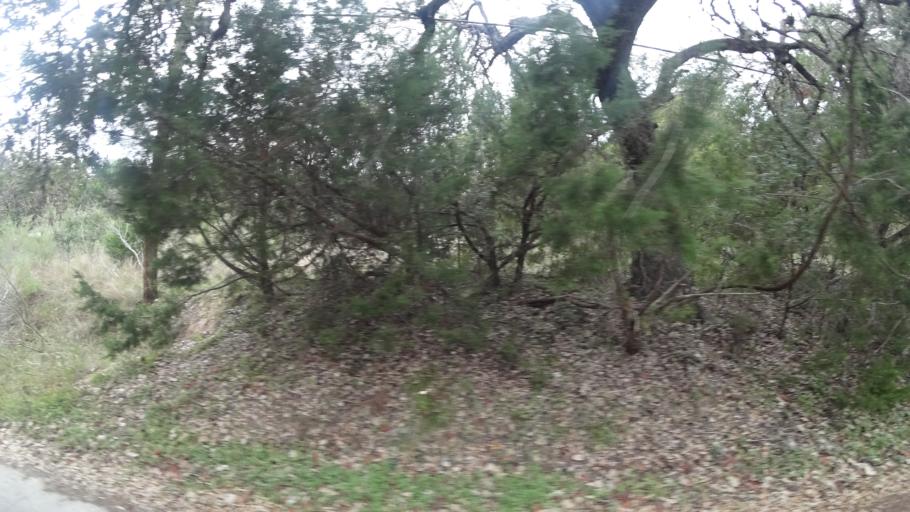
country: US
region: Texas
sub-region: Travis County
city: Hudson Bend
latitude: 30.3691
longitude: -97.9157
